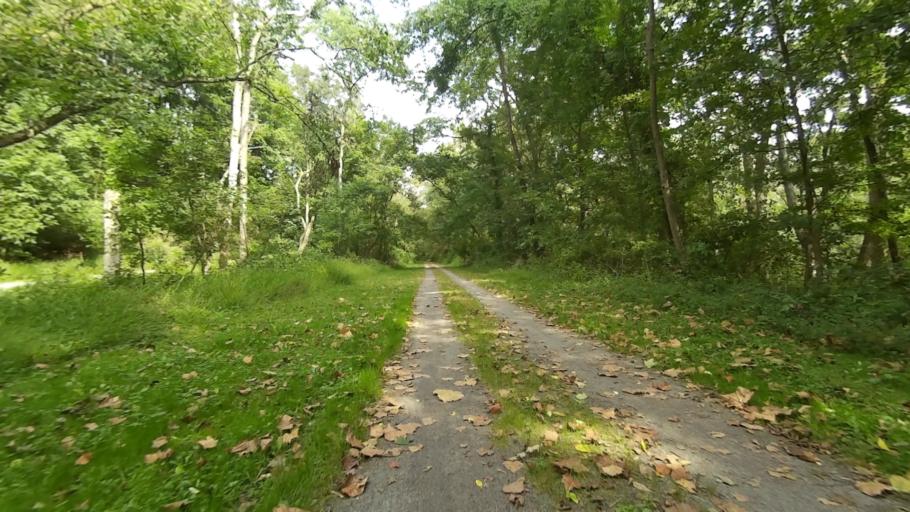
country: US
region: Pennsylvania
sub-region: Blair County
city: Williamsburg
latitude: 40.5130
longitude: -78.1696
